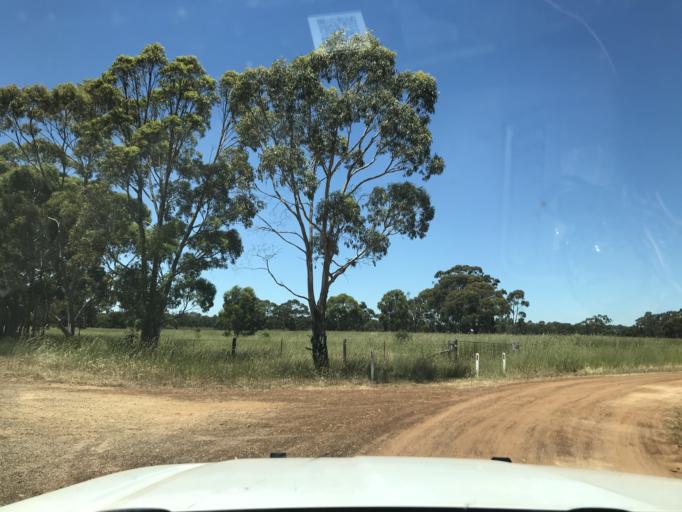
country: AU
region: South Australia
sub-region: Wattle Range
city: Penola
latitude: -37.0397
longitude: 141.3825
